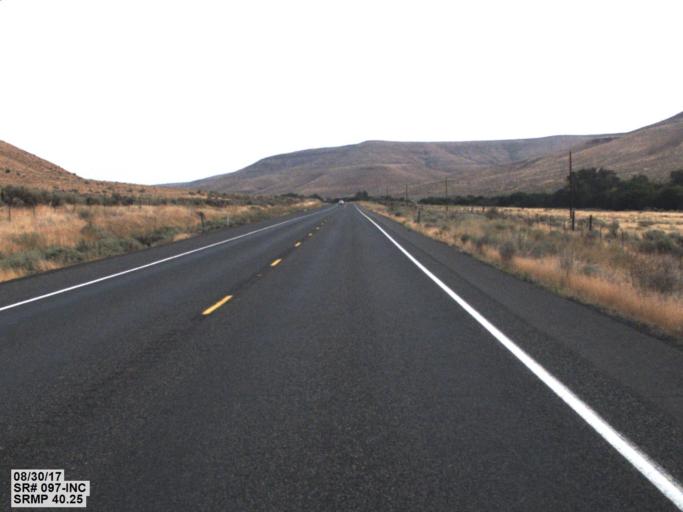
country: US
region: Washington
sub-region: Yakima County
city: Toppenish
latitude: 46.1311
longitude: -120.5274
